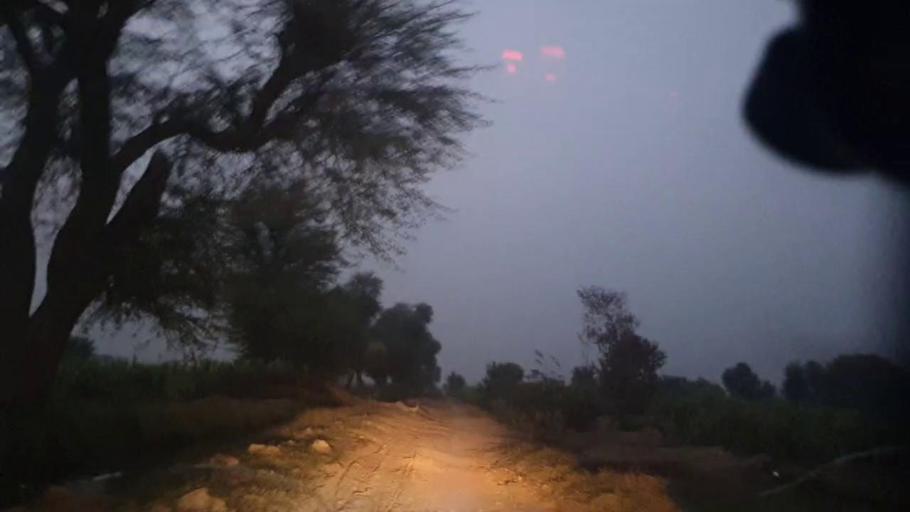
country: PK
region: Sindh
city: Hingorja
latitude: 27.2052
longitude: 68.3715
